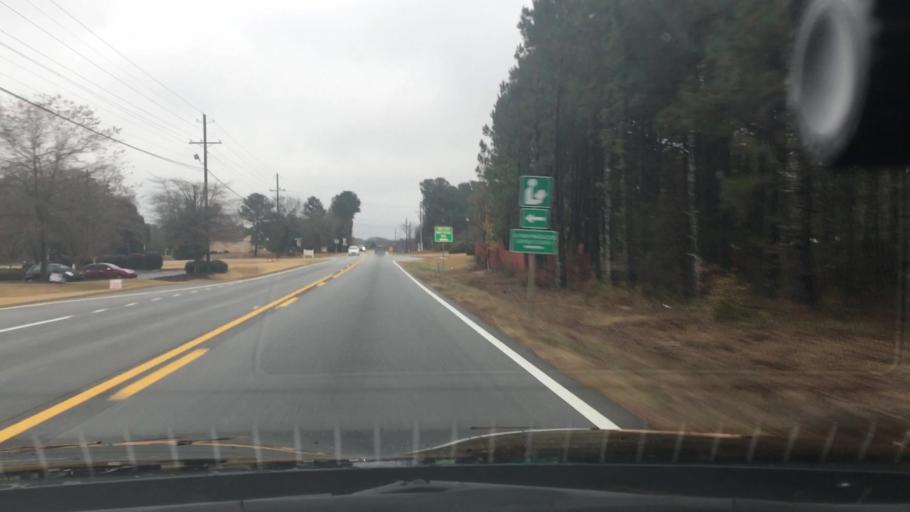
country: US
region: Georgia
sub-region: Fayette County
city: Peachtree City
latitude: 33.3861
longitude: -84.6739
